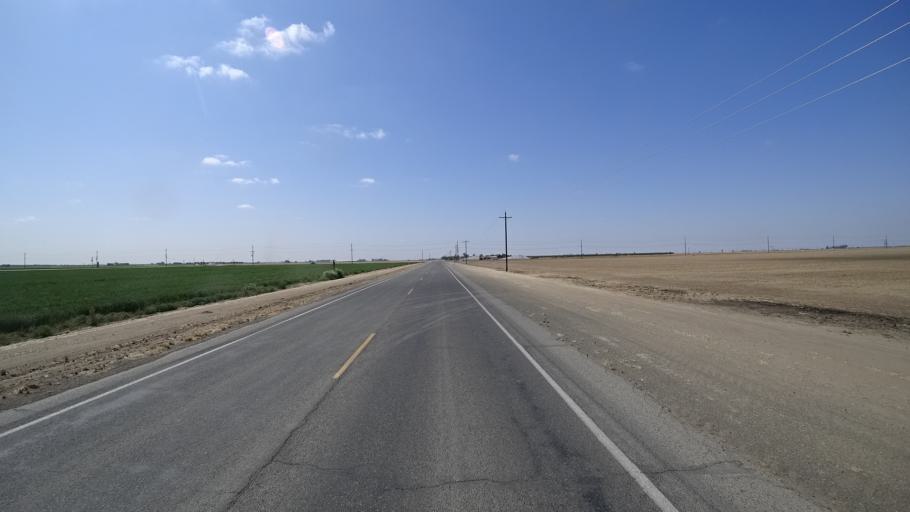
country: US
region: California
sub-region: Kings County
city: Home Garden
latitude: 36.2577
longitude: -119.6369
